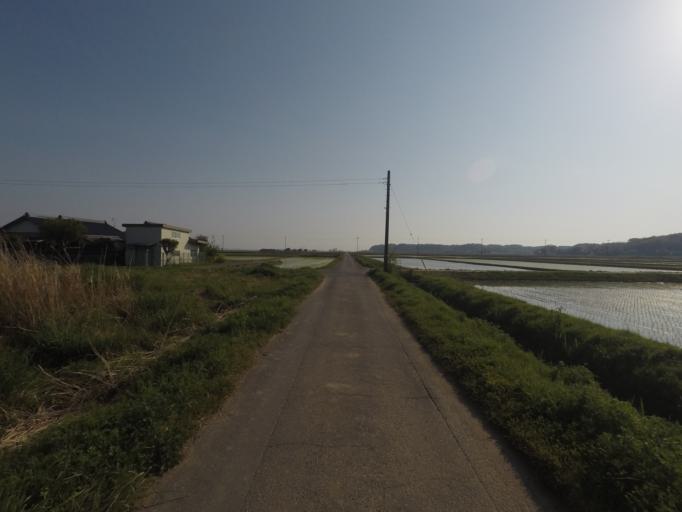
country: JP
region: Ibaraki
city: Inashiki
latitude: 36.0848
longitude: 140.3888
